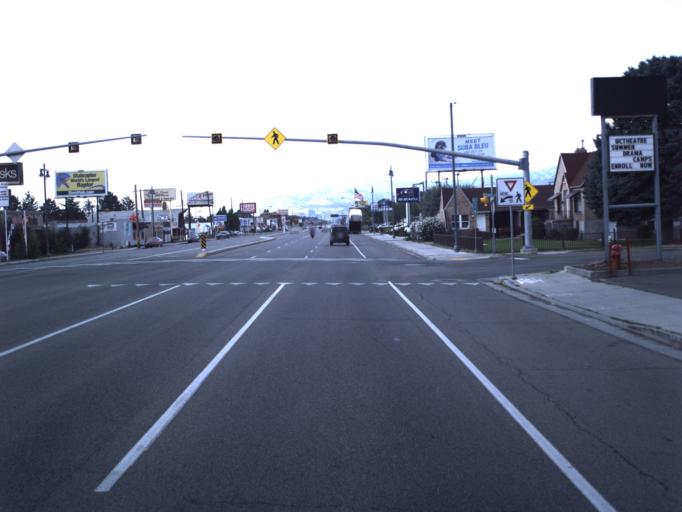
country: US
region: Utah
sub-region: Salt Lake County
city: Centerfield
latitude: 40.6926
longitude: -111.8882
